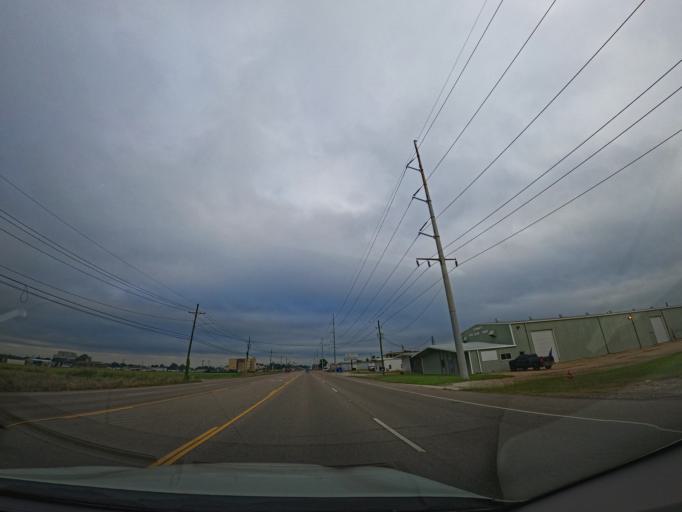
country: US
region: Louisiana
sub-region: Terrebonne Parish
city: Presquille
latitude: 29.5650
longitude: -90.6821
